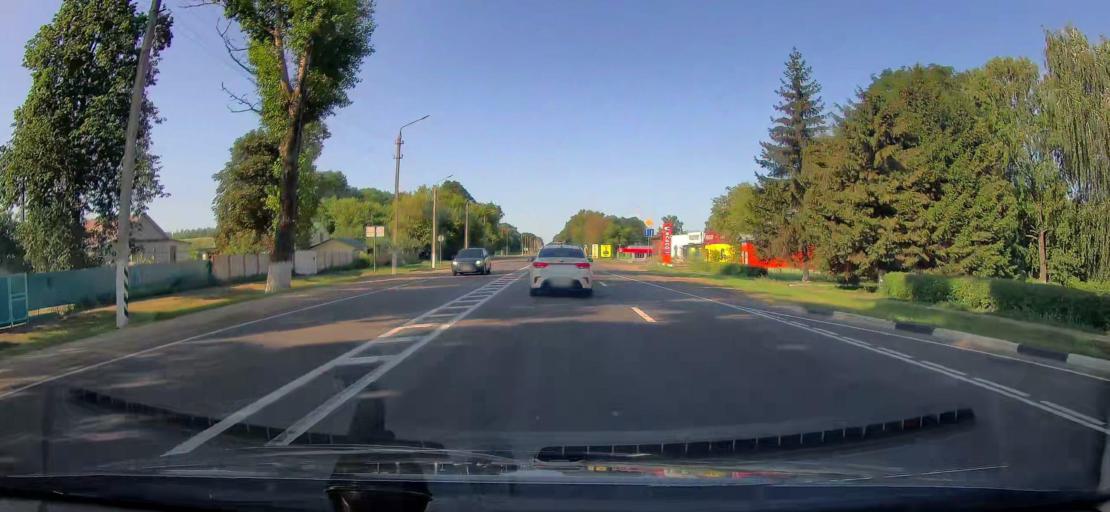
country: RU
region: Orjol
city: Mtsensk
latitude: 53.1813
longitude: 36.4094
